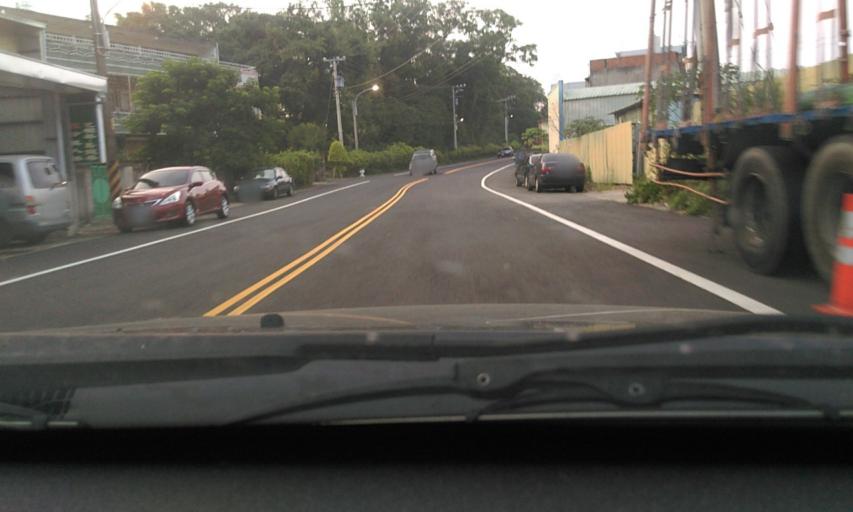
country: TW
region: Taiwan
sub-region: Hsinchu
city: Hsinchu
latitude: 24.6887
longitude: 120.9891
